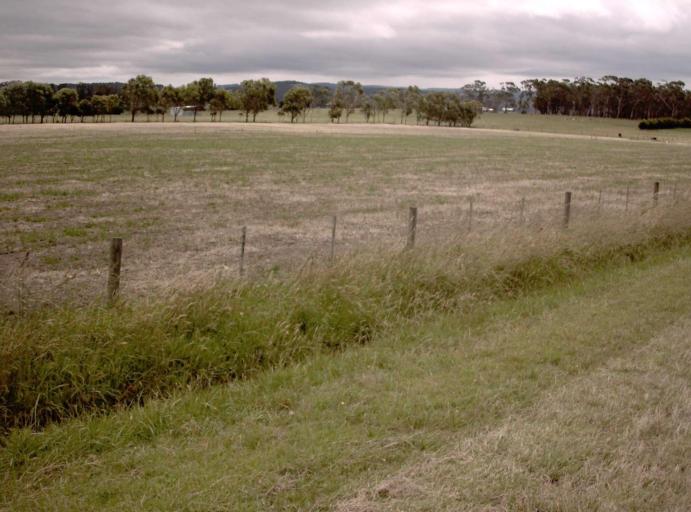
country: AU
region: Victoria
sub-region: Latrobe
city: Traralgon
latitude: -38.5470
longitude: 146.6553
